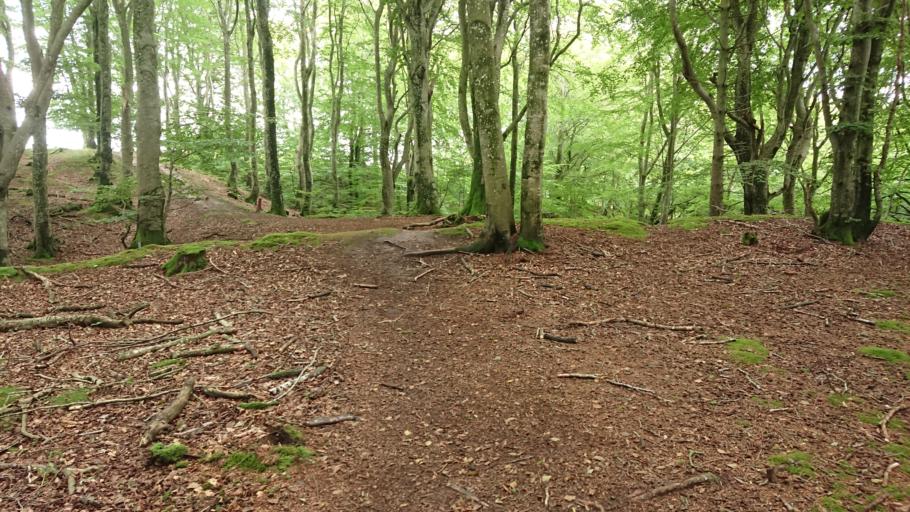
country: DK
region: North Denmark
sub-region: Hjorring Kommune
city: Sindal
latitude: 57.4810
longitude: 10.1619
